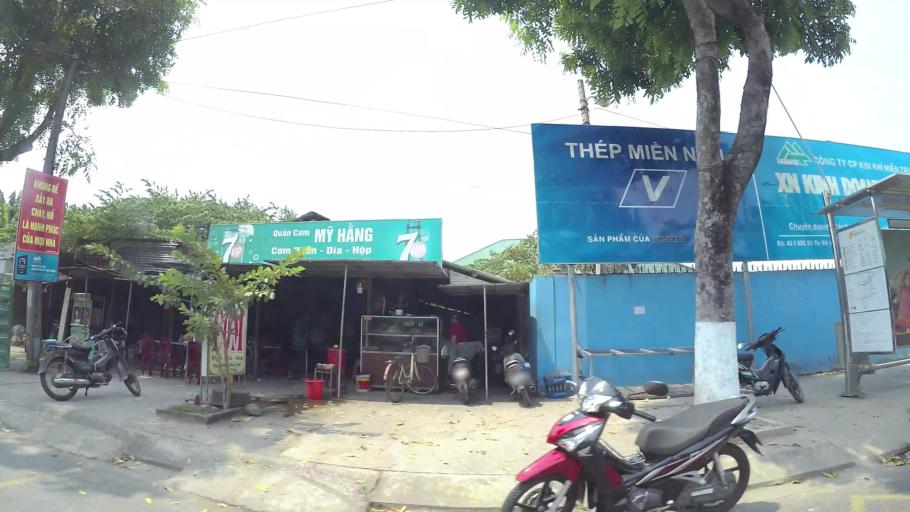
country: VN
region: Da Nang
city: Cam Le
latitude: 15.9815
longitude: 108.2080
